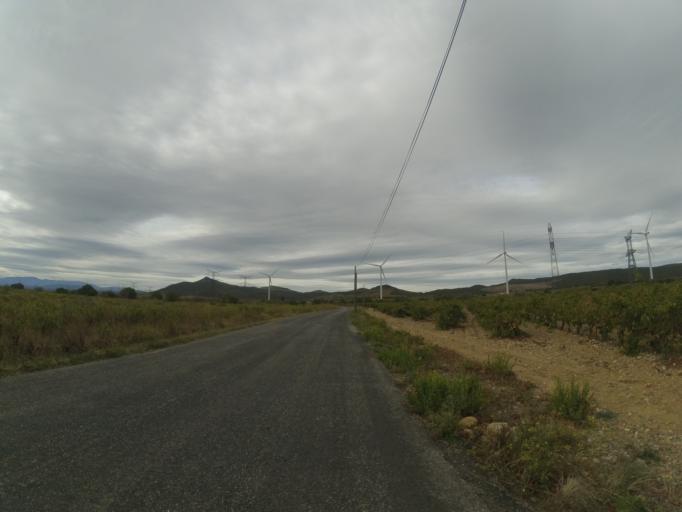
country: FR
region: Languedoc-Roussillon
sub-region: Departement des Pyrenees-Orientales
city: Corneilla-la-Riviere
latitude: 42.7182
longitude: 2.7495
